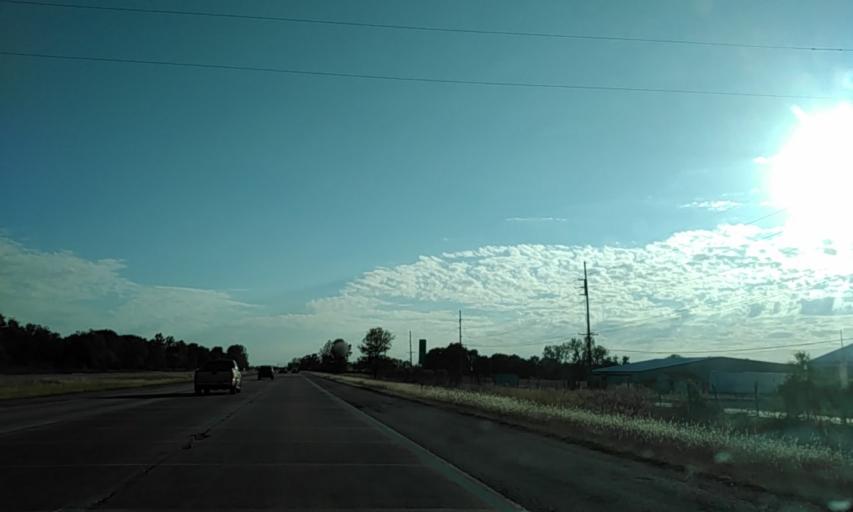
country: US
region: Illinois
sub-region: Saint Clair County
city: Dupo
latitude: 38.4998
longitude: -90.2117
